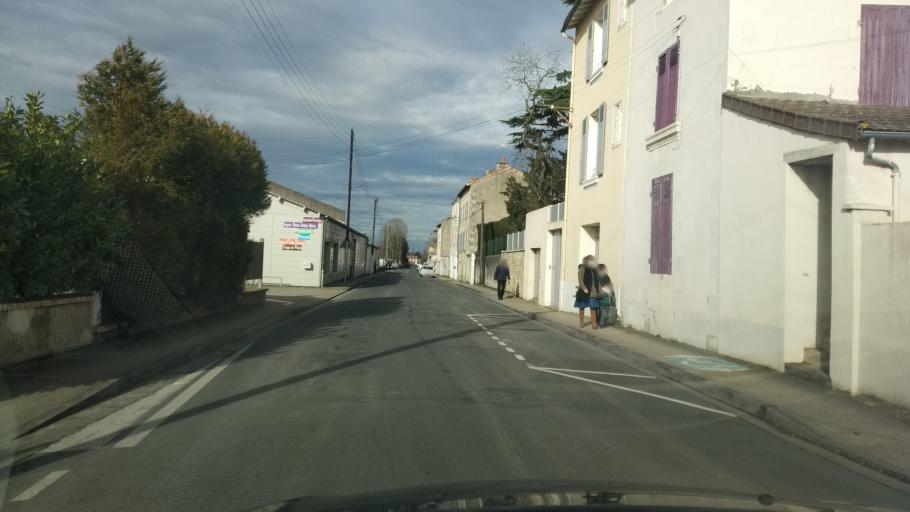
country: FR
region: Poitou-Charentes
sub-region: Departement de la Vienne
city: Poitiers
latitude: 46.5956
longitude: 0.3416
